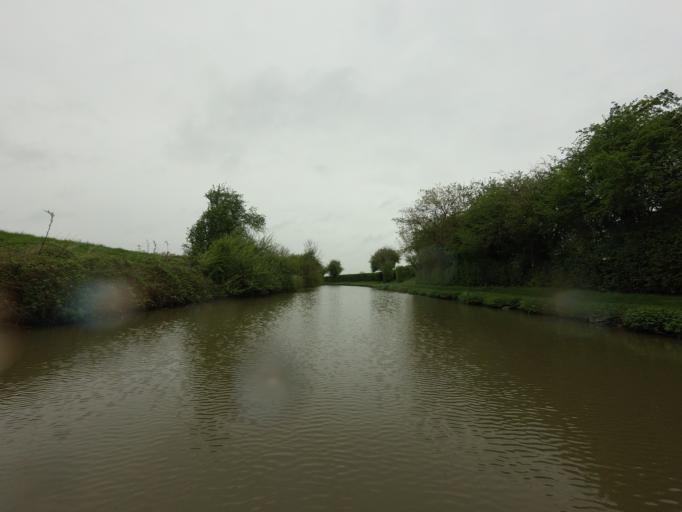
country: GB
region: England
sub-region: Milton Keynes
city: Castlethorpe
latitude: 52.0919
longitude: -0.8604
